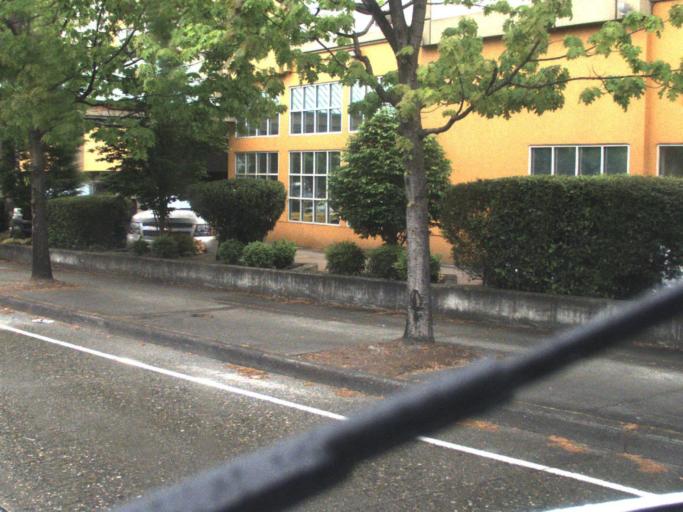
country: US
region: Washington
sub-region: Pierce County
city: Fife
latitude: 47.2419
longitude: -122.3570
